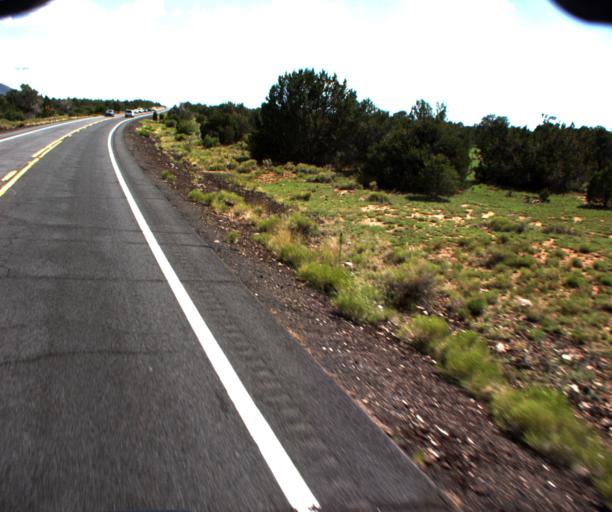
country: US
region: Arizona
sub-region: Coconino County
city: Williams
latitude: 35.4564
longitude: -112.1704
